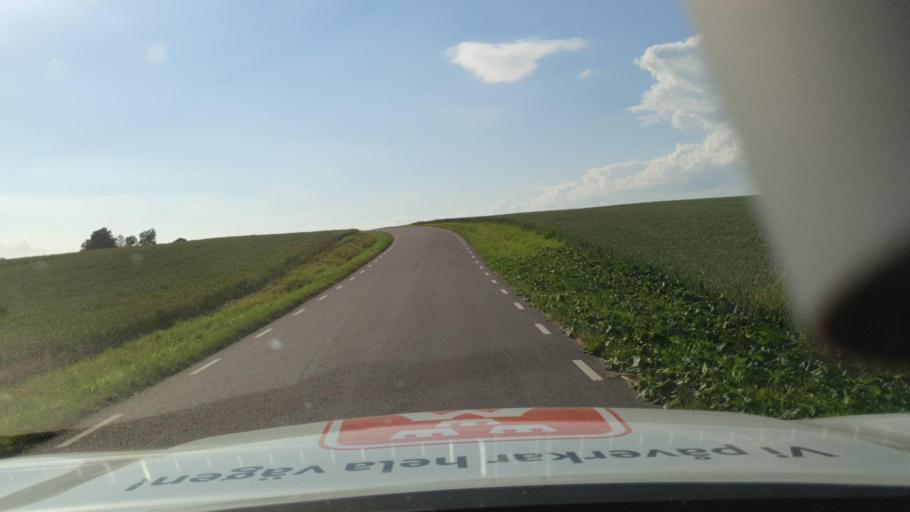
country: SE
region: Skane
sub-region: Skurups Kommun
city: Rydsgard
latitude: 55.5051
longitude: 13.5686
